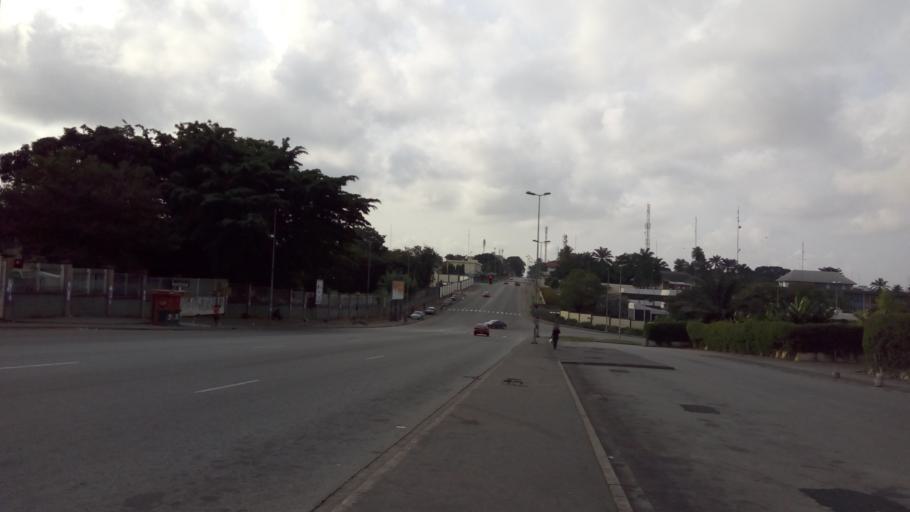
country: CI
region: Lagunes
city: Abidjan
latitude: 5.3334
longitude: -4.0216
